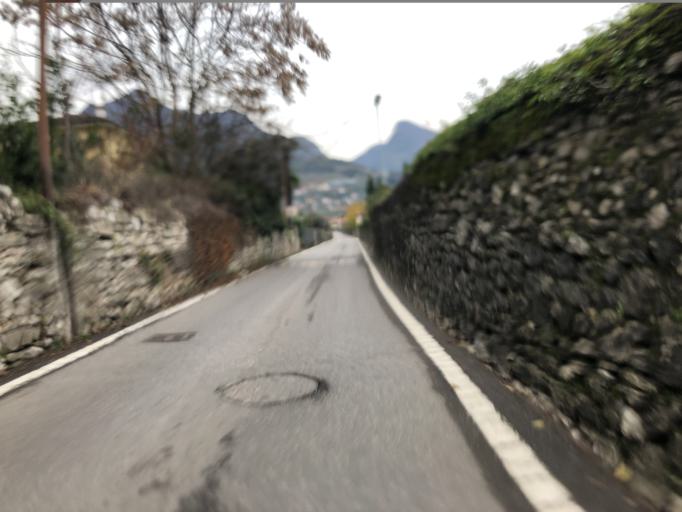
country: IT
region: Trentino-Alto Adige
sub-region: Provincia di Trento
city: Riva del Garda
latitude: 45.9015
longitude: 10.8389
